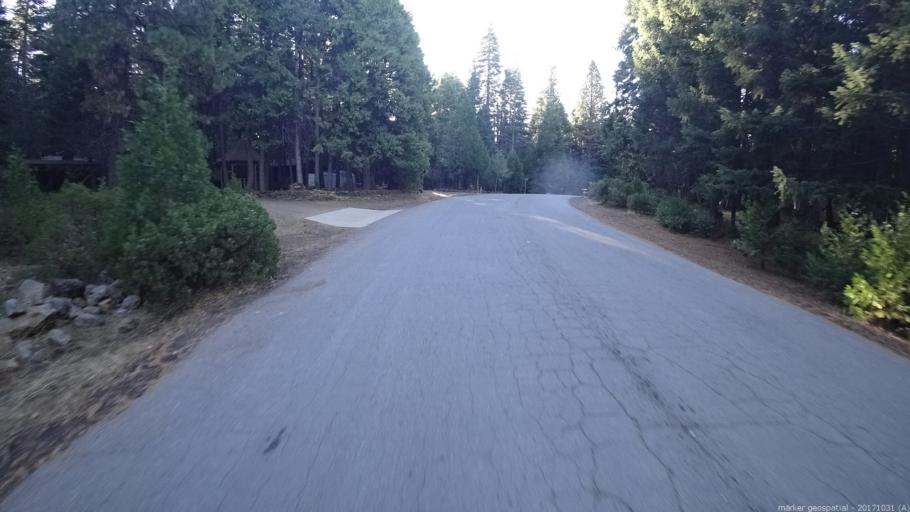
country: US
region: California
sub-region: Shasta County
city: Shingletown
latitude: 40.5217
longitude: -121.7956
